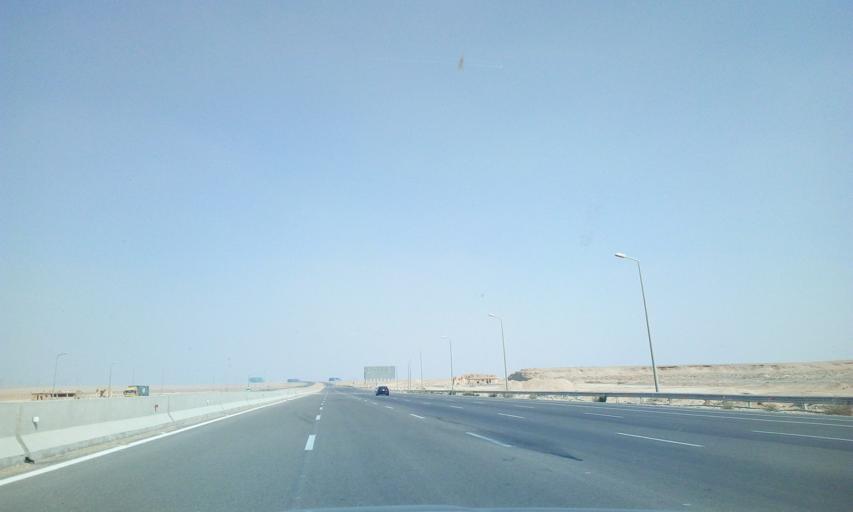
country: EG
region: Muhafazat al Qahirah
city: Halwan
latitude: 29.9032
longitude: 31.7622
